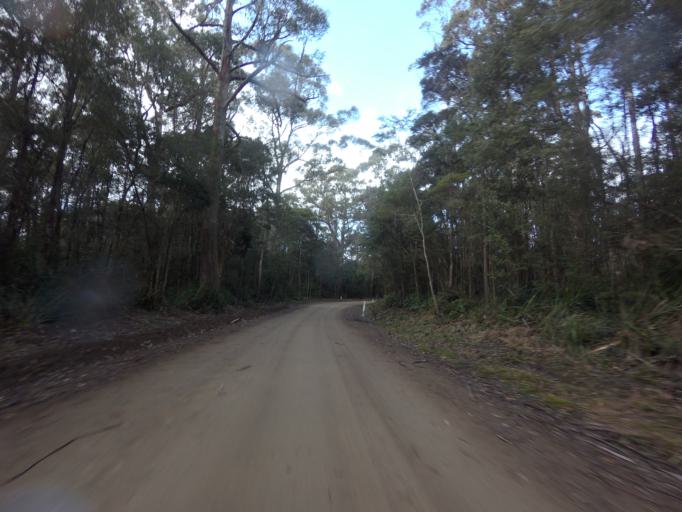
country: AU
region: Tasmania
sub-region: Huon Valley
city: Geeveston
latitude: -43.5755
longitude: 146.8883
